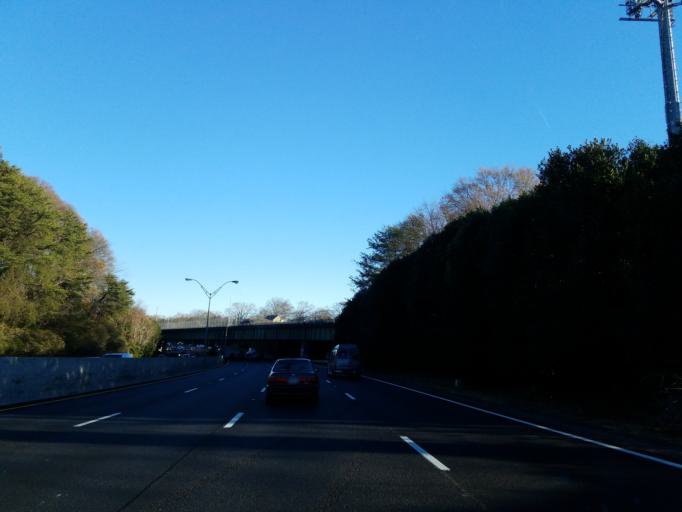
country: US
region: Georgia
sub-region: Fulton County
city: Atlanta
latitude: 33.7482
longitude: -84.4409
